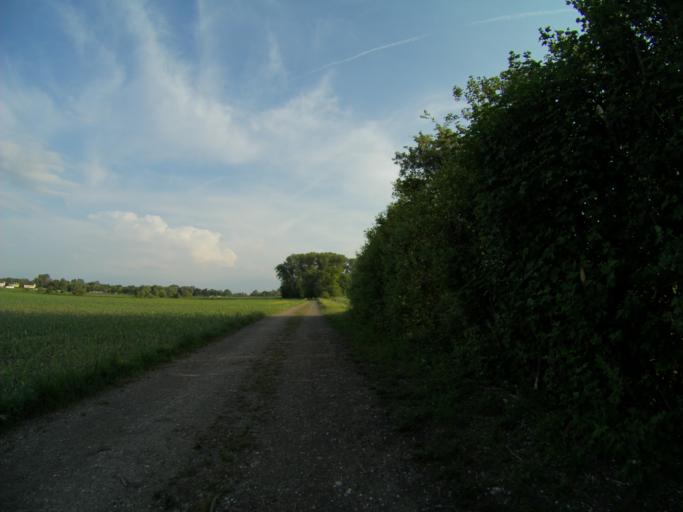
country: DE
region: Bavaria
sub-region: Upper Bavaria
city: Freising
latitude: 48.3781
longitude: 11.7677
